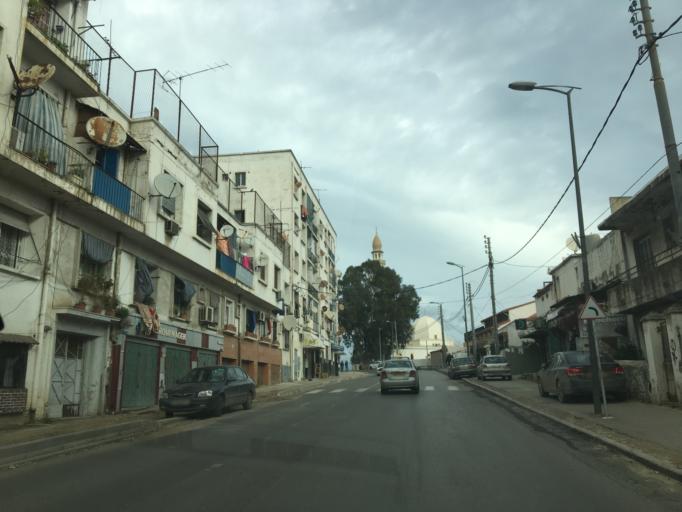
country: DZ
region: Alger
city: Algiers
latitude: 36.7740
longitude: 3.0425
